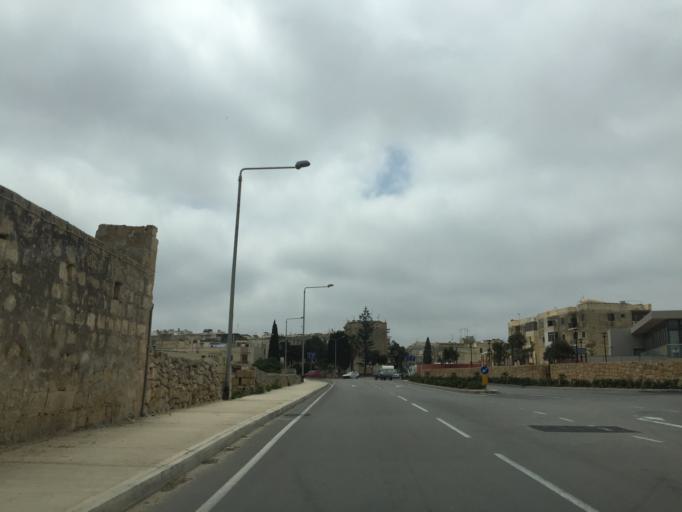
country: MT
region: Ir-Rabat
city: Rabat
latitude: 35.8848
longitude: 14.3909
